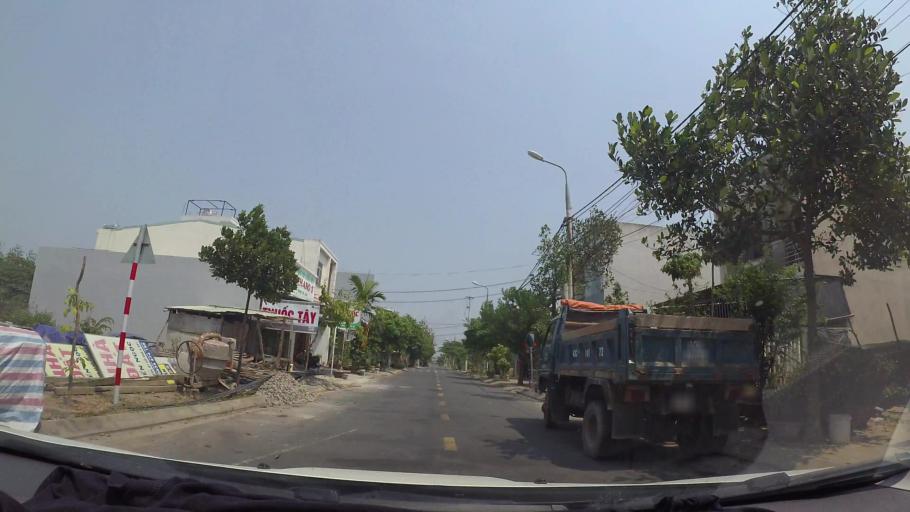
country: VN
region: Da Nang
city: Cam Le
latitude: 15.9958
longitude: 108.2024
